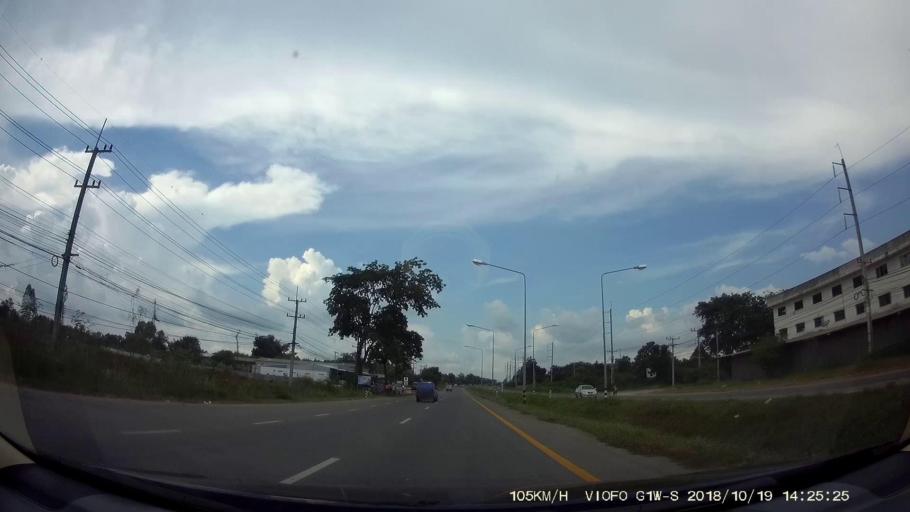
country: TH
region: Chaiyaphum
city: Kaeng Khro
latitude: 16.0935
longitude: 102.2651
